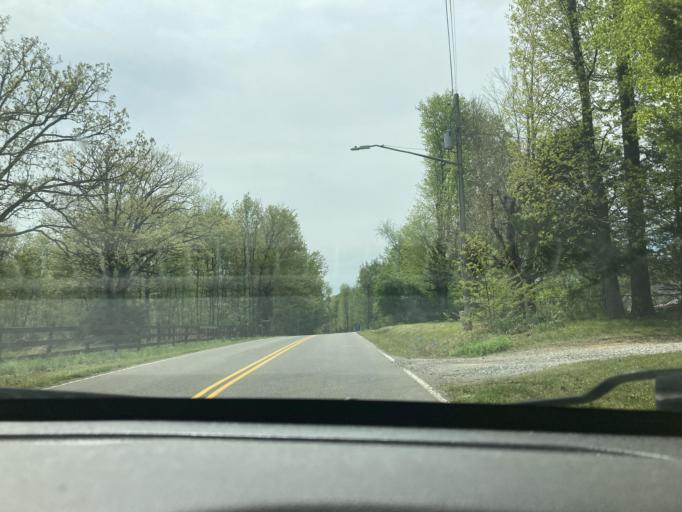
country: US
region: Tennessee
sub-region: Dickson County
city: Dickson
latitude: 36.1057
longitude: -87.3771
